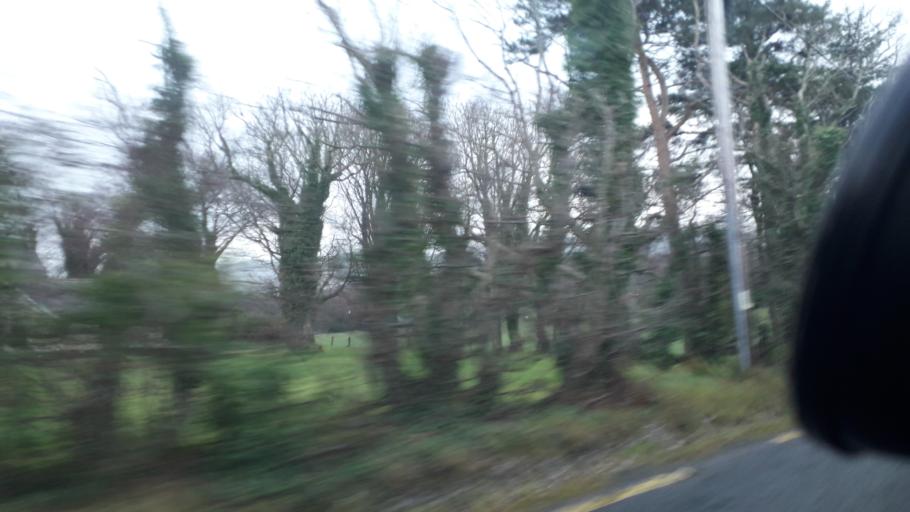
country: IE
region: Ulster
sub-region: County Donegal
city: Ramelton
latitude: 55.1965
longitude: -7.6391
